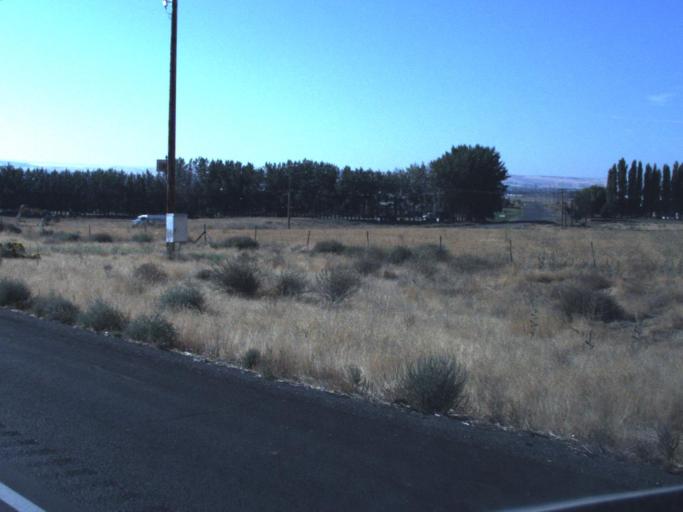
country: US
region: Washington
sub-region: Franklin County
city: Pasco
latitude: 46.2865
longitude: -119.0939
